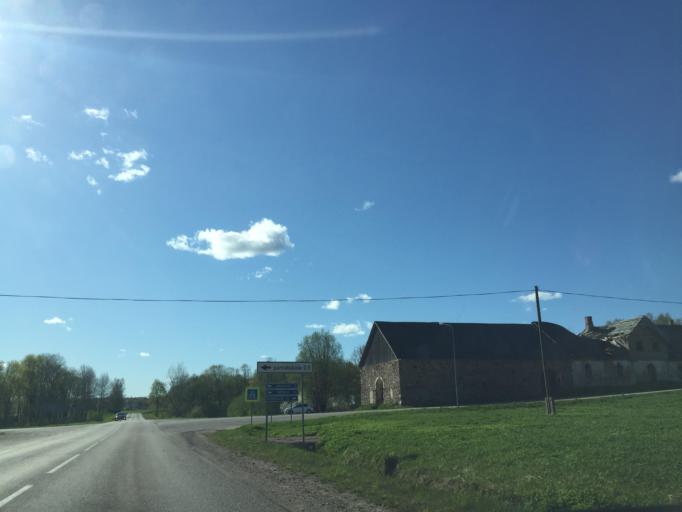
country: LV
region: Madonas Rajons
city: Madona
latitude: 56.8064
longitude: 26.0331
